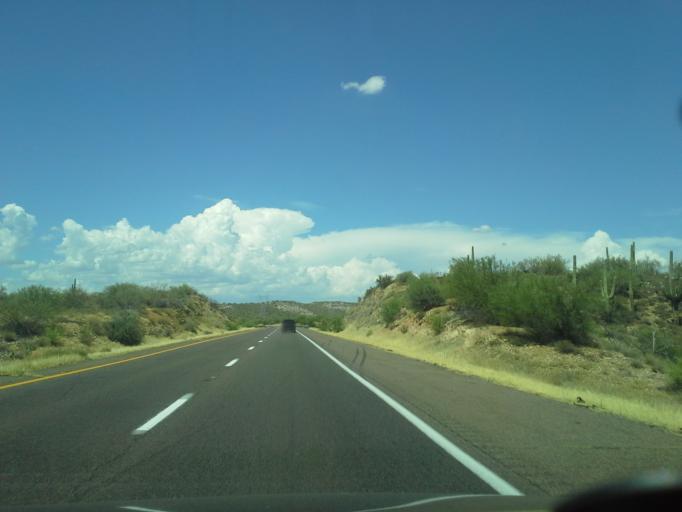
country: US
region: Arizona
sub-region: Yavapai County
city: Black Canyon City
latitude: 34.0023
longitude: -112.1341
